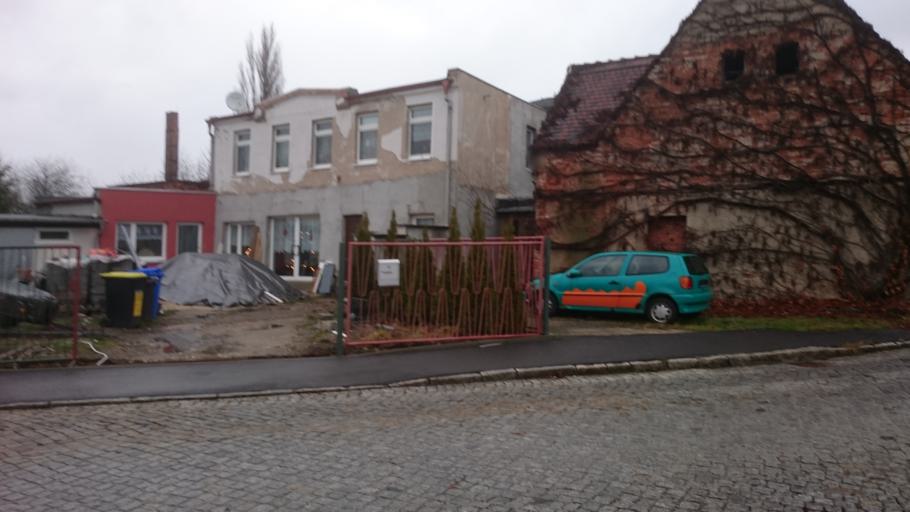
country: DE
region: Saxony
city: Zwickau
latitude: 50.7410
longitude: 12.4944
